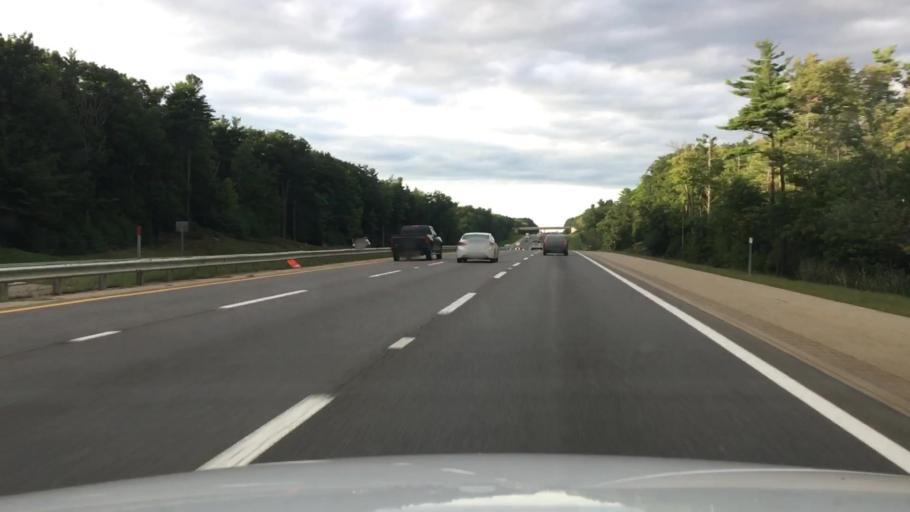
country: US
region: Maine
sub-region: York County
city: Ogunquit
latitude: 43.2631
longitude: -70.6191
